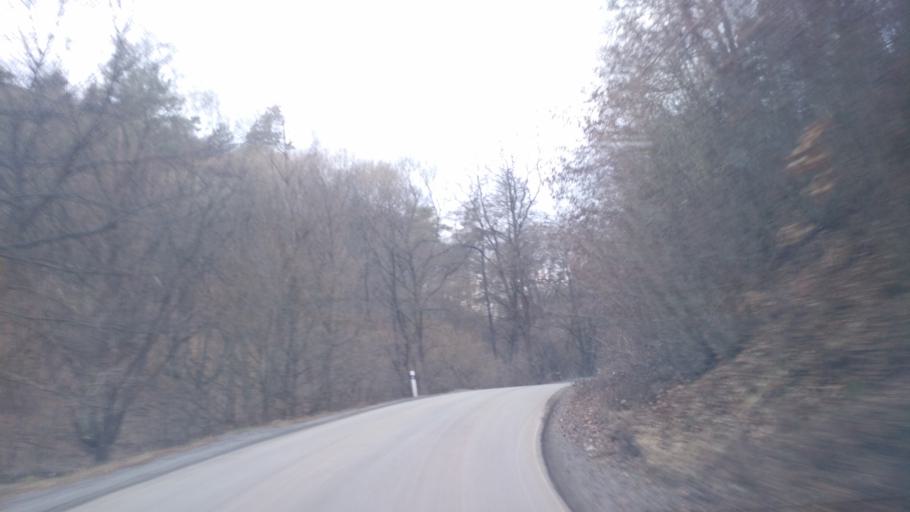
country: SK
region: Presovsky
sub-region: Okres Presov
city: Presov
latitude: 48.8970
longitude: 21.2015
